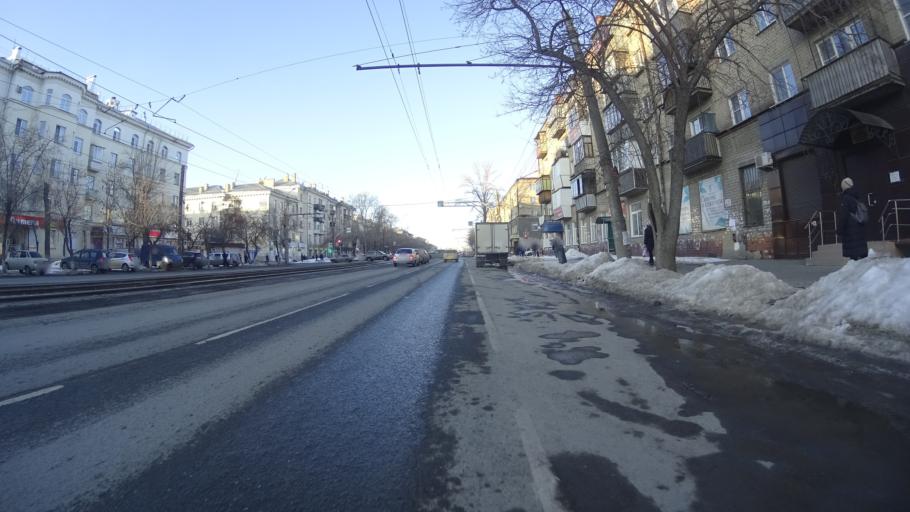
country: RU
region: Chelyabinsk
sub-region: Gorod Chelyabinsk
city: Chelyabinsk
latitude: 55.1409
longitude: 61.4422
